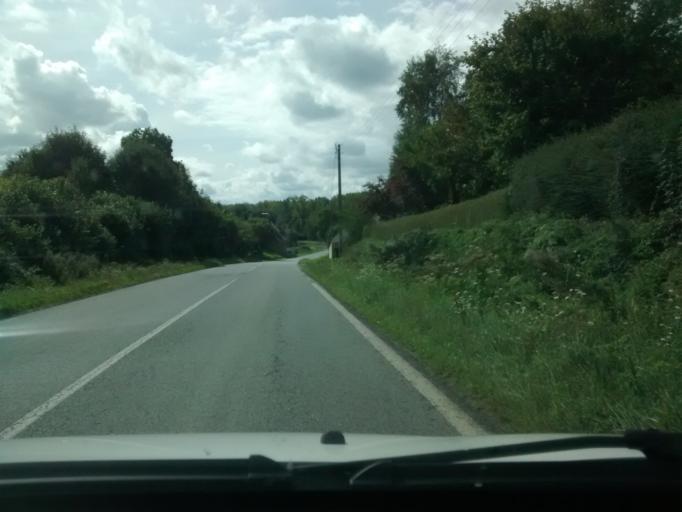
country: FR
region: Brittany
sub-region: Departement d'Ille-et-Vilaine
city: Plerguer
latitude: 48.5156
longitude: -1.8569
